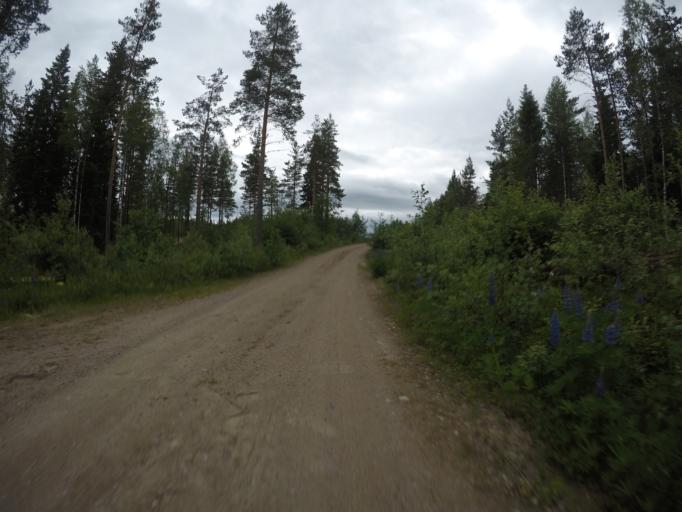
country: SE
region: Dalarna
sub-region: Ludvika Kommun
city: Abborrberget
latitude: 60.0741
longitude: 14.5624
